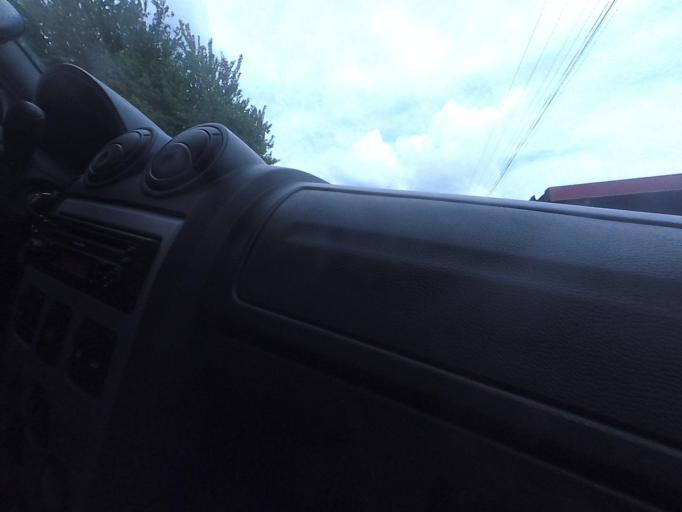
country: RO
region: Neamt
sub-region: Comuna Cordun
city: Pildesti
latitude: 46.9820
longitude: 26.8050
